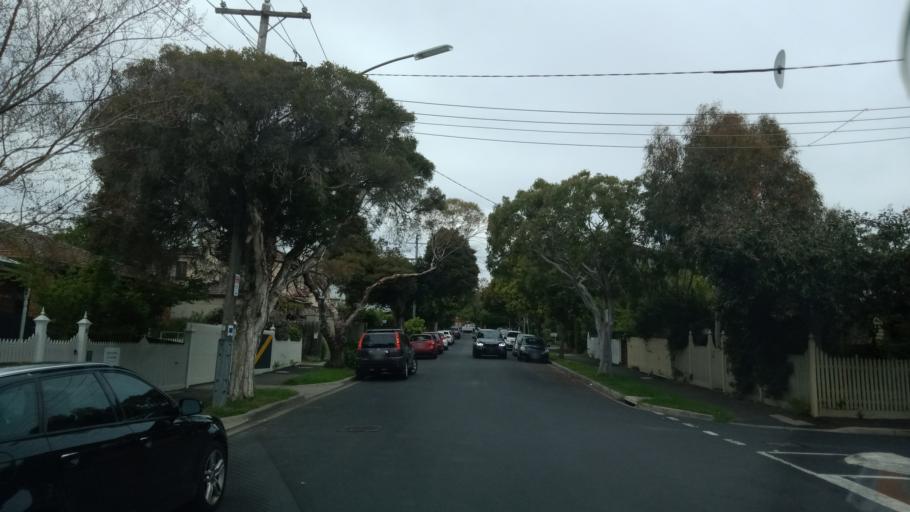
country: AU
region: Victoria
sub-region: Boroondara
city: Hawthorn East
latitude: -37.8280
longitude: 145.0383
